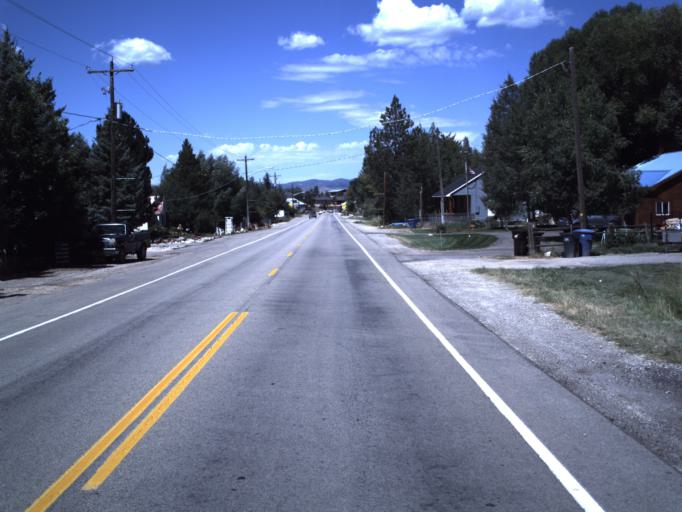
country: US
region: Utah
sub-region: Summit County
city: Oakley
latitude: 40.7103
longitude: -111.2952
